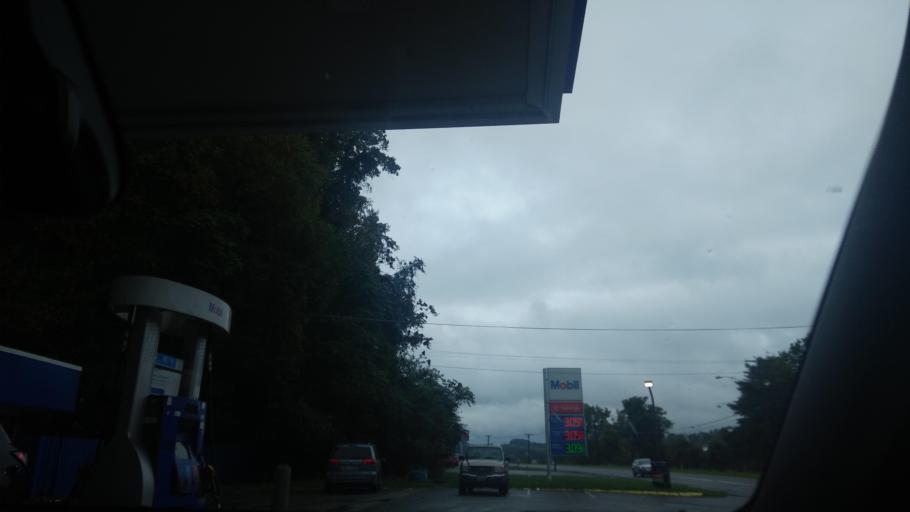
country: US
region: Virginia
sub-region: City of Galax
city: Galax
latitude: 36.6507
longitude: -80.9189
